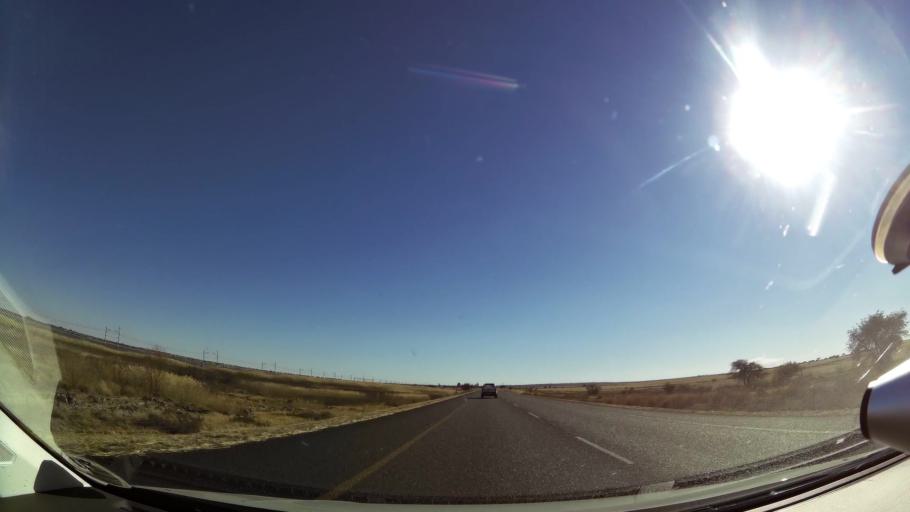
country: ZA
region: Northern Cape
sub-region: Frances Baard District Municipality
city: Kimberley
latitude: -28.6779
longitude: 24.7775
